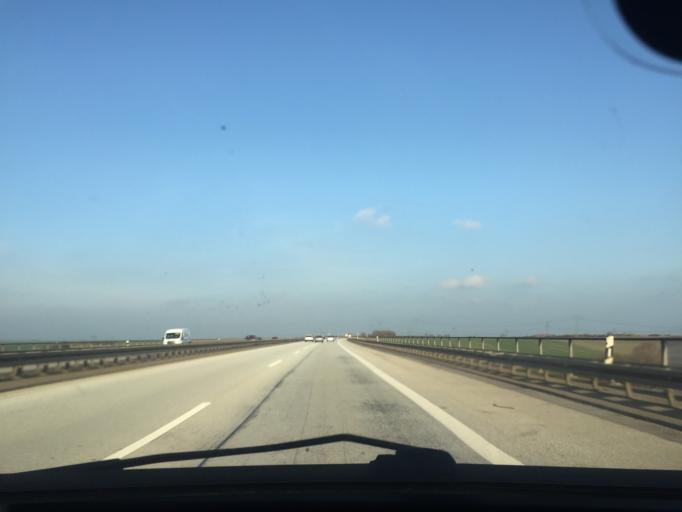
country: DE
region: Saxony-Anhalt
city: Hohendodeleben
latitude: 52.1225
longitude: 11.5301
